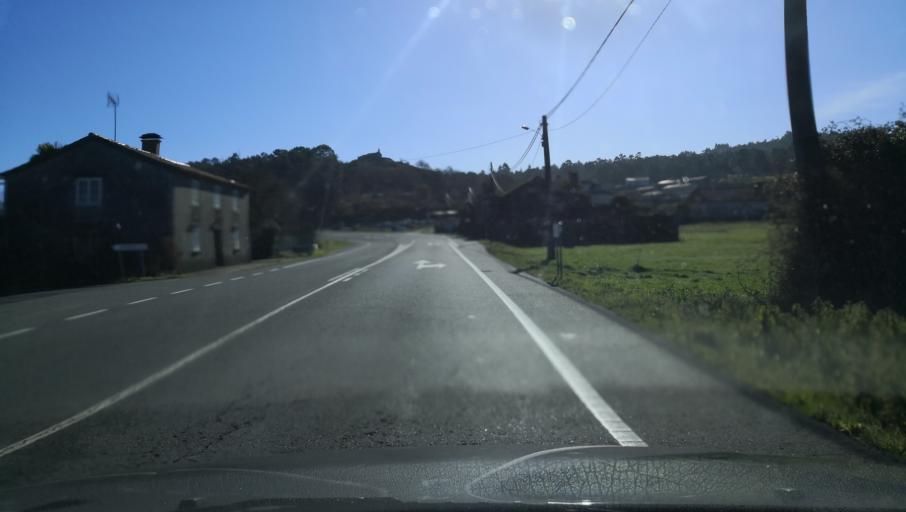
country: ES
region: Galicia
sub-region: Provincia da Coruna
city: Ribeira
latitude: 42.7491
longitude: -8.3474
